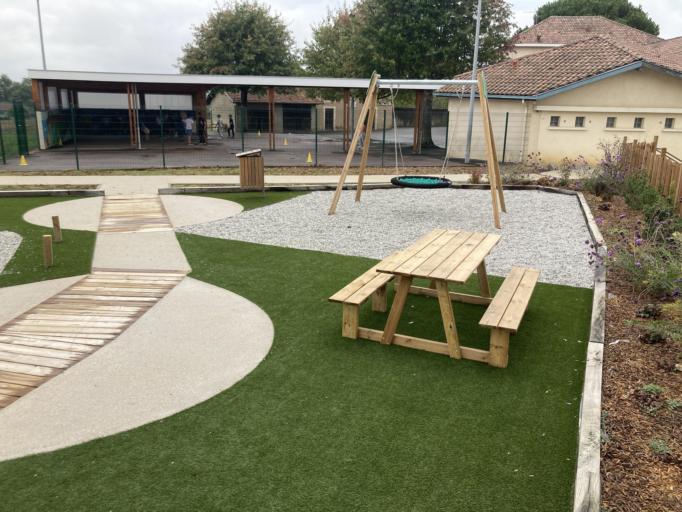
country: FR
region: Aquitaine
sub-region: Departement des Landes
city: Montfort-en-Chalosse
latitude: 43.7326
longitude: -0.8745
